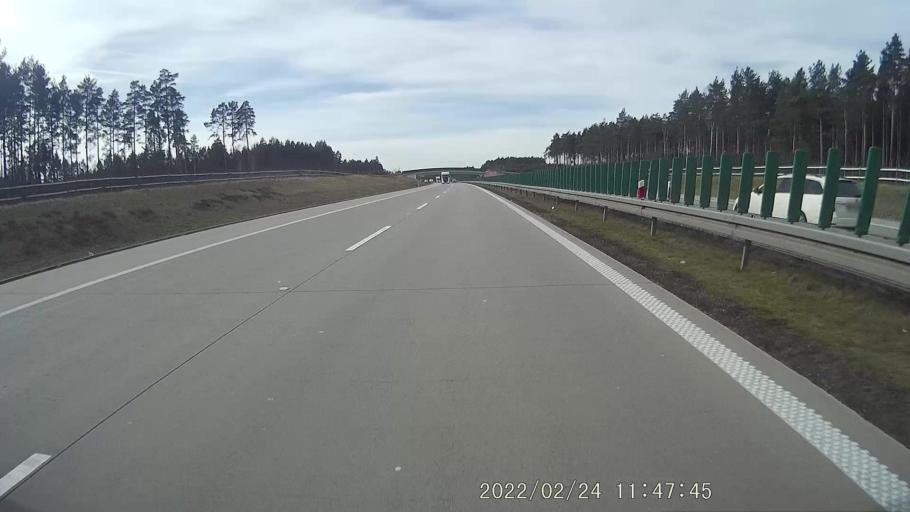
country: PL
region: Lower Silesian Voivodeship
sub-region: Powiat polkowicki
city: Radwanice
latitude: 51.5779
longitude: 15.9523
